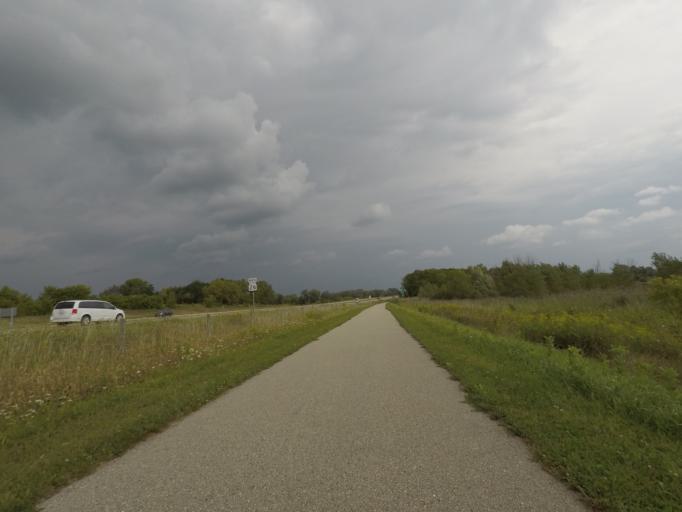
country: US
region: Wisconsin
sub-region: Jefferson County
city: Fort Atkinson
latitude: 42.9605
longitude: -88.8274
